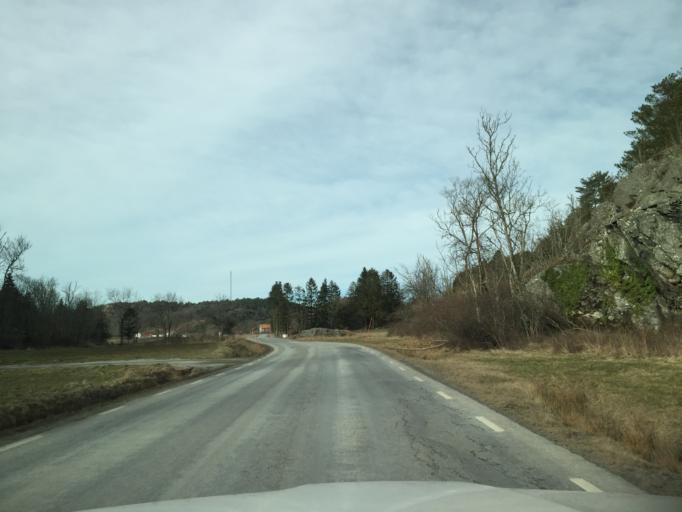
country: SE
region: Vaestra Goetaland
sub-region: Tjorns Kommun
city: Skaerhamn
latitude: 58.0320
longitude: 11.5941
